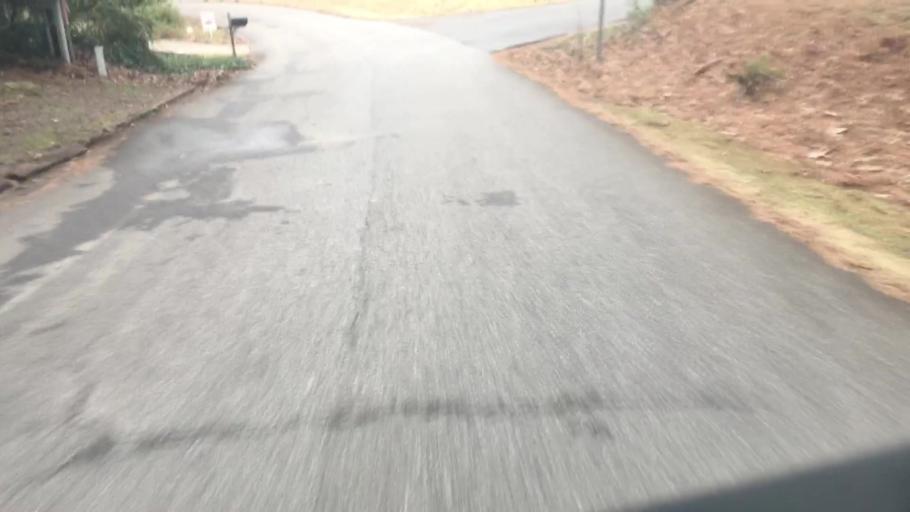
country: US
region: Alabama
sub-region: Jefferson County
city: Vestavia Hills
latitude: 33.4184
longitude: -86.7615
